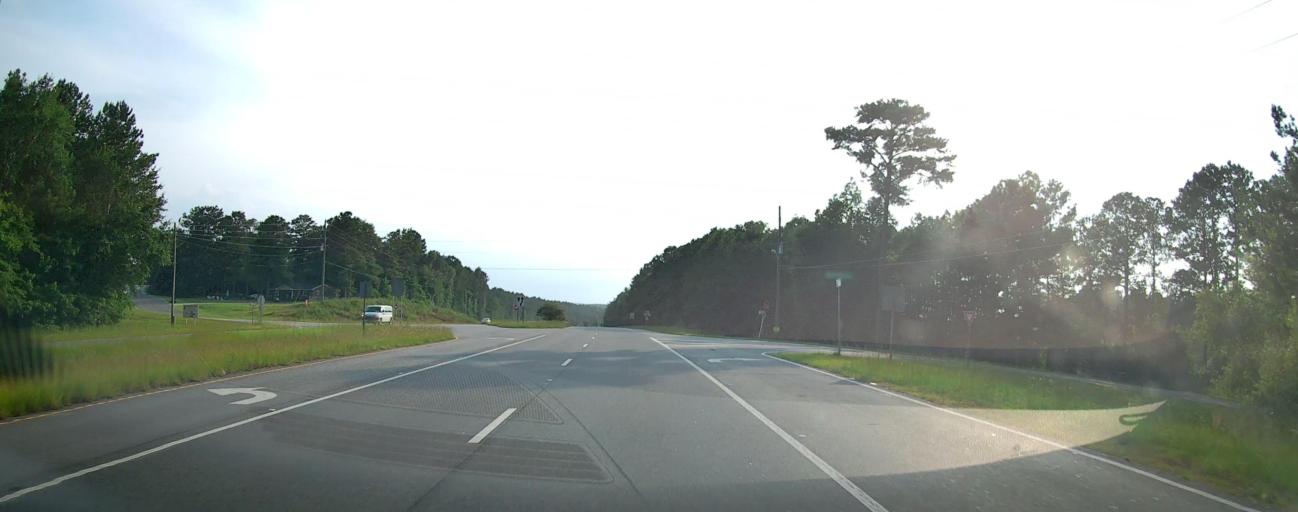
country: US
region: Georgia
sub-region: Talbot County
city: Talbotton
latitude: 32.5488
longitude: -84.7031
